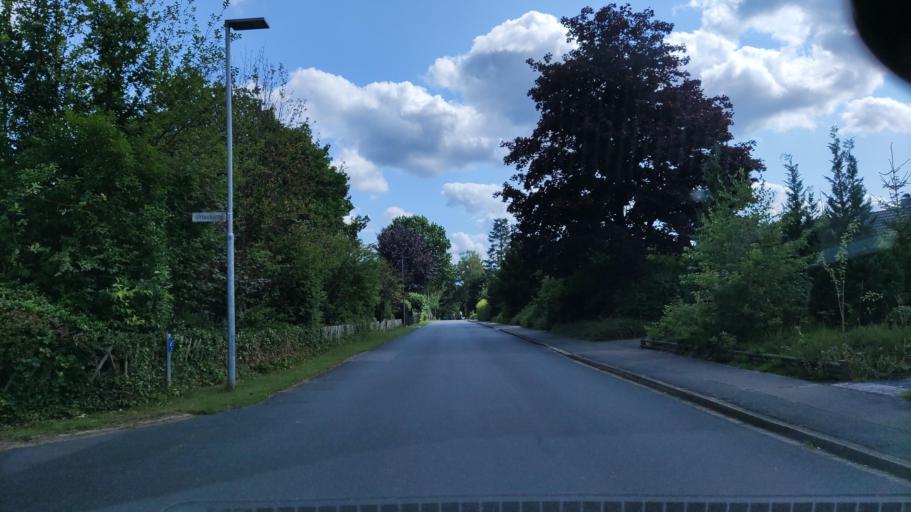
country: DE
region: Lower Saxony
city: Soltau
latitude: 53.0171
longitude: 9.8730
